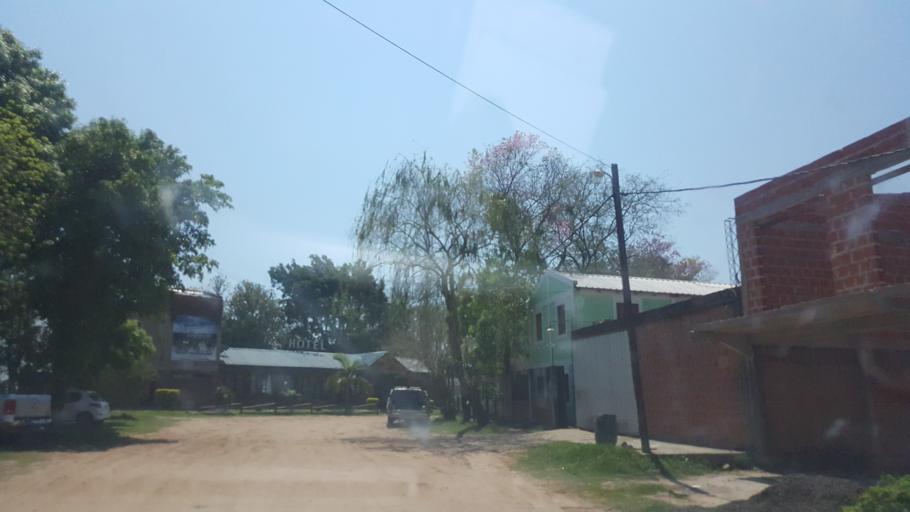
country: AR
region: Corrientes
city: Ita Ibate
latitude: -27.4241
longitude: -57.3373
